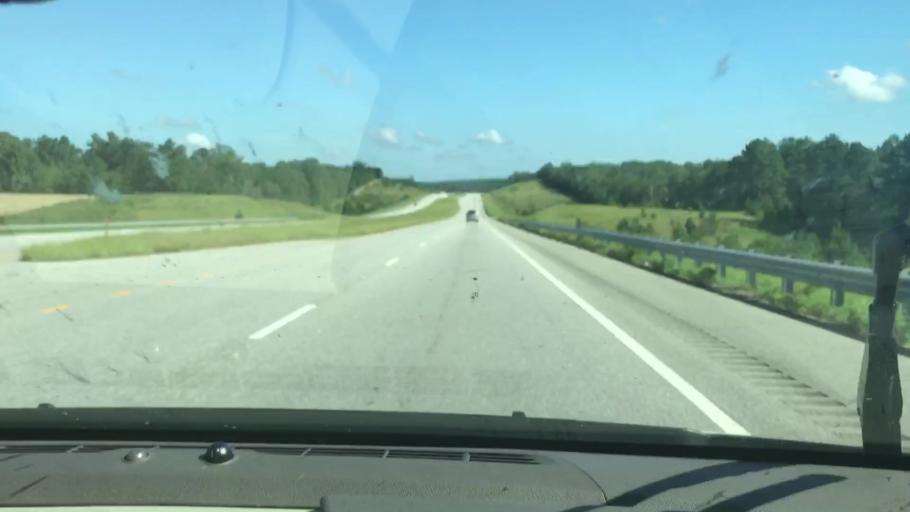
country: US
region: Alabama
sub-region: Barbour County
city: Eufaula
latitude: 32.0993
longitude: -85.1499
